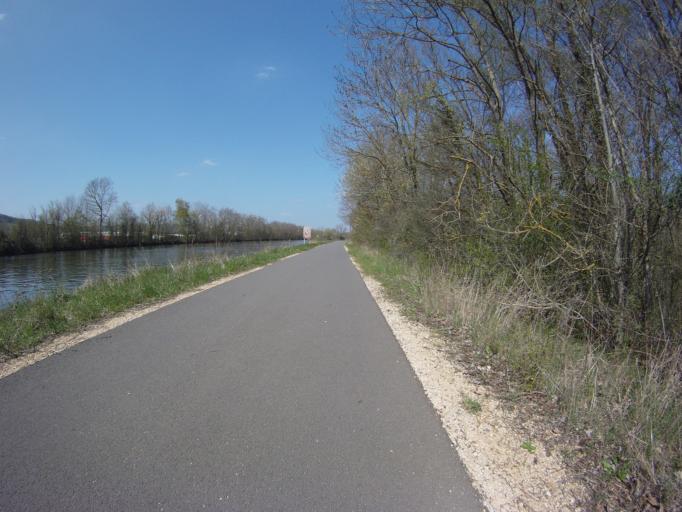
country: FR
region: Lorraine
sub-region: Departement de Meurthe-et-Moselle
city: Dieulouard
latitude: 48.8666
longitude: 6.0732
